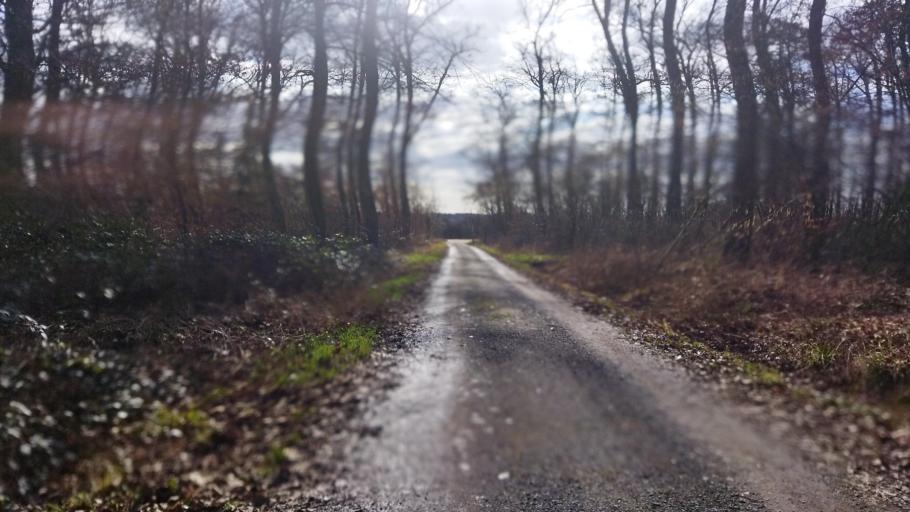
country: DE
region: Baden-Wuerttemberg
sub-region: Regierungsbezirk Stuttgart
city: Freudental
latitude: 48.9927
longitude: 9.0590
